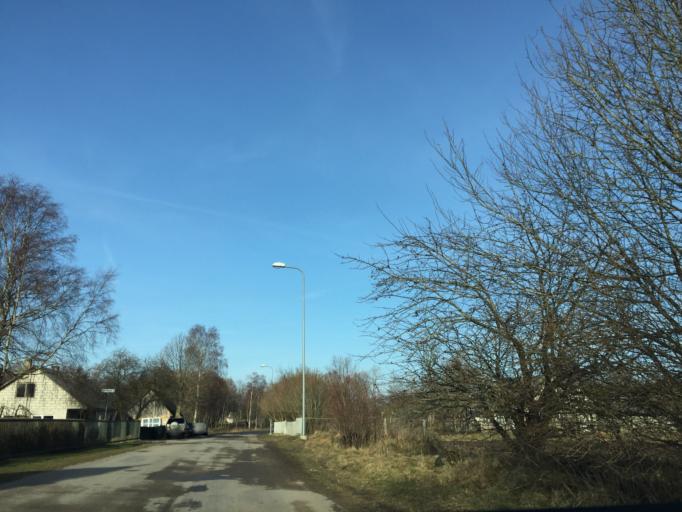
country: EE
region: Saare
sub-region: Kuressaare linn
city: Kuressaare
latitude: 58.3640
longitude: 22.0350
